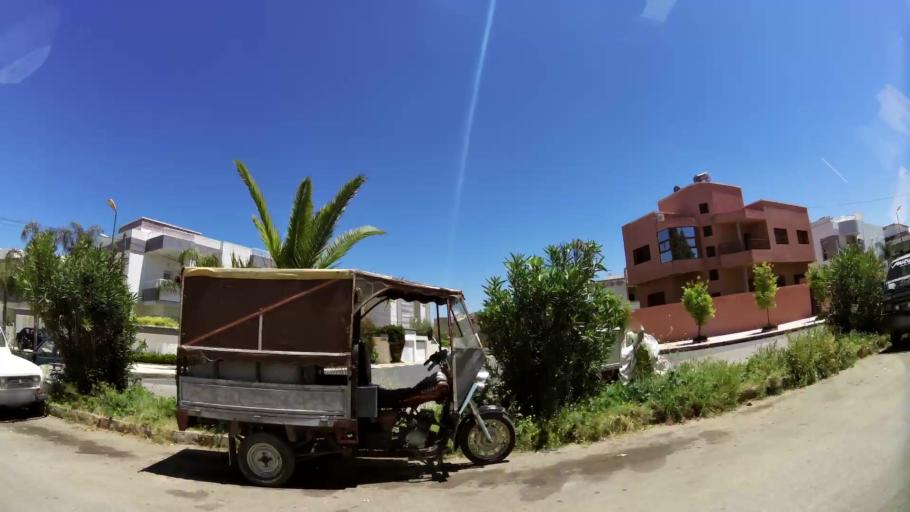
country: MA
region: Meknes-Tafilalet
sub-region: Meknes
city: Meknes
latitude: 33.9092
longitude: -5.5598
